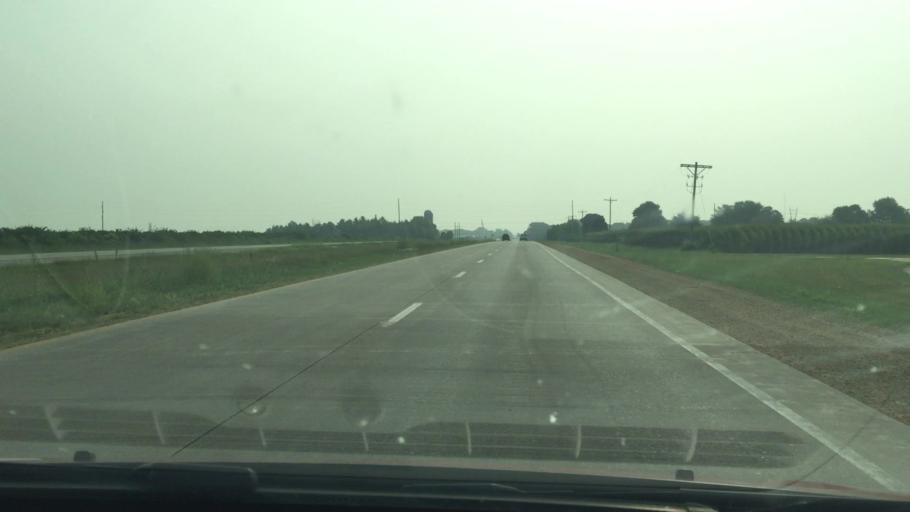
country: US
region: Iowa
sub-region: Scott County
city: Buffalo
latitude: 41.5088
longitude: -90.7124
